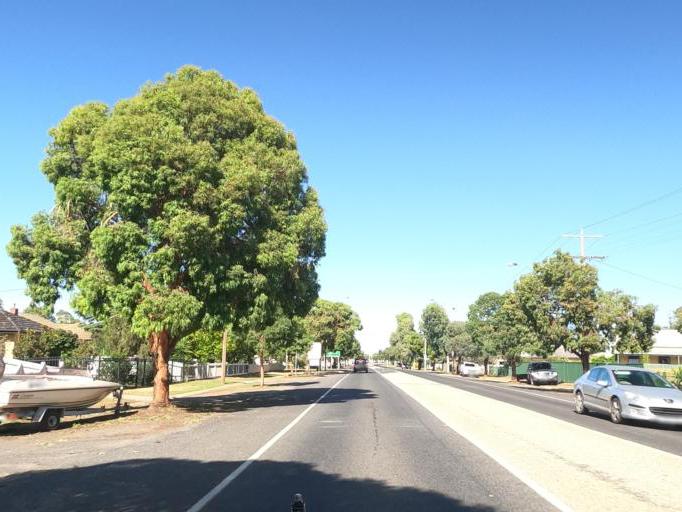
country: AU
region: Victoria
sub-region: Moira
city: Yarrawonga
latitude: -36.0166
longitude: 146.0084
